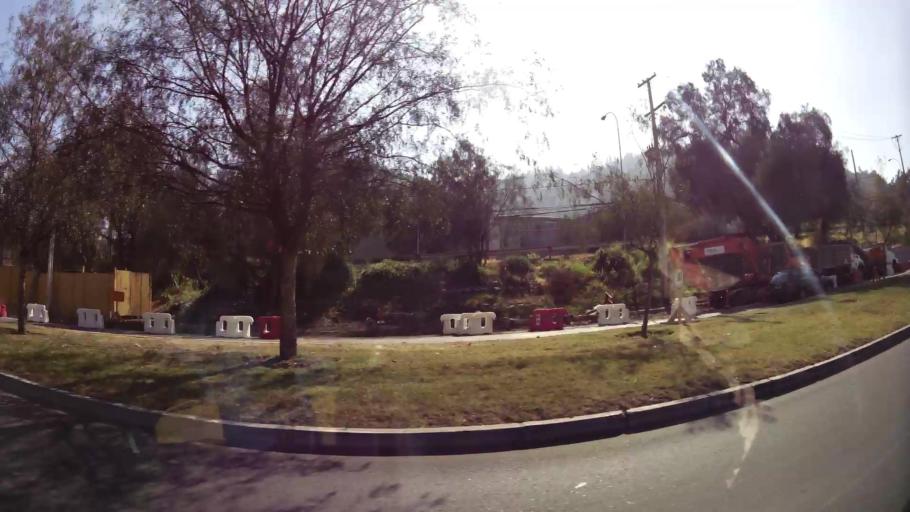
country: CL
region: Santiago Metropolitan
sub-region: Provincia de Santiago
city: Santiago
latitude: -33.4271
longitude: -70.6235
